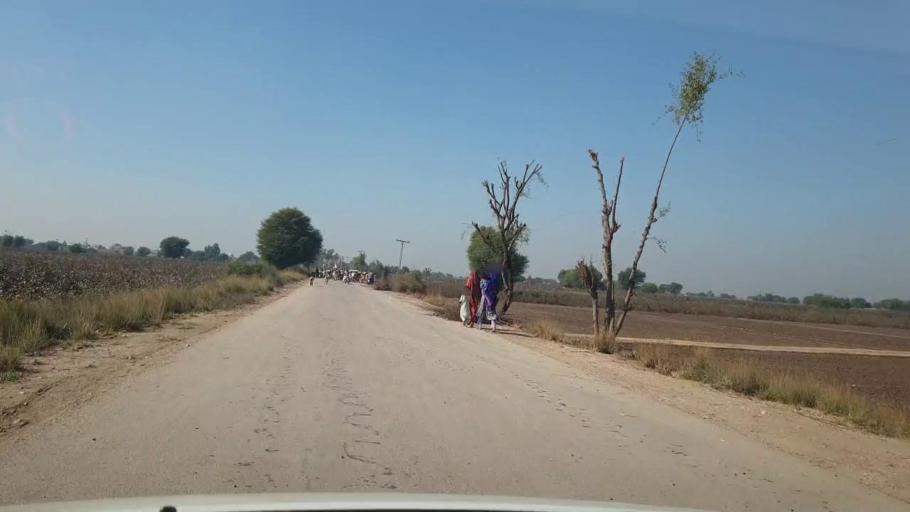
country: PK
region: Sindh
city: Bhan
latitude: 26.6458
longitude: 67.7239
